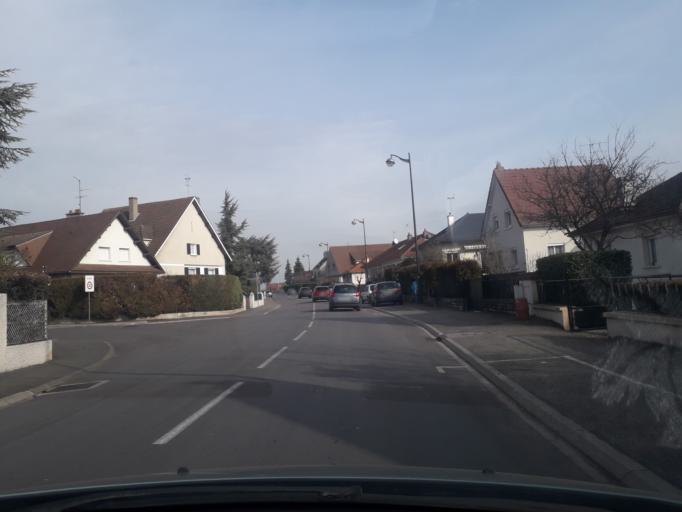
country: FR
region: Bourgogne
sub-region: Departement de la Cote-d'Or
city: Fontaine-les-Dijon
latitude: 47.3436
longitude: 5.0234
